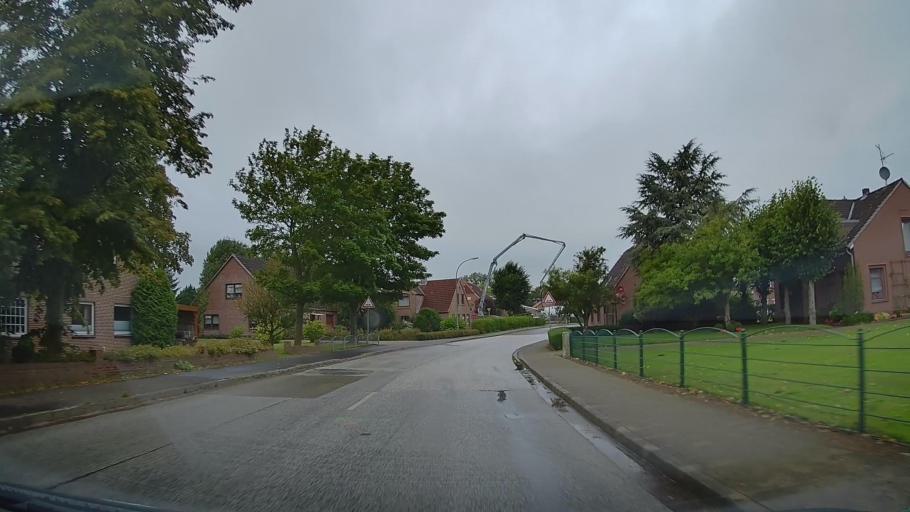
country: DE
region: Schleswig-Holstein
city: Brokdorf
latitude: 53.8637
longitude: 9.3194
